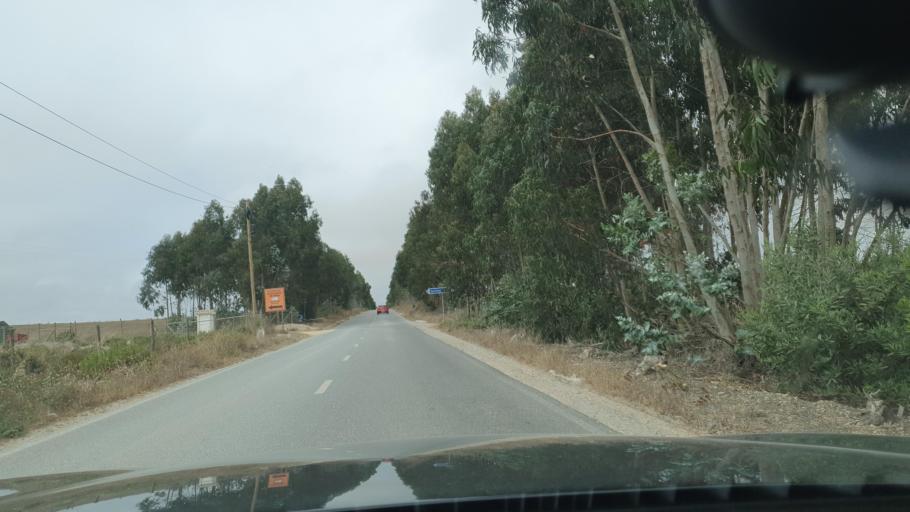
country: PT
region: Beja
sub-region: Odemira
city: Sao Teotonio
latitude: 37.5341
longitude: -8.7552
